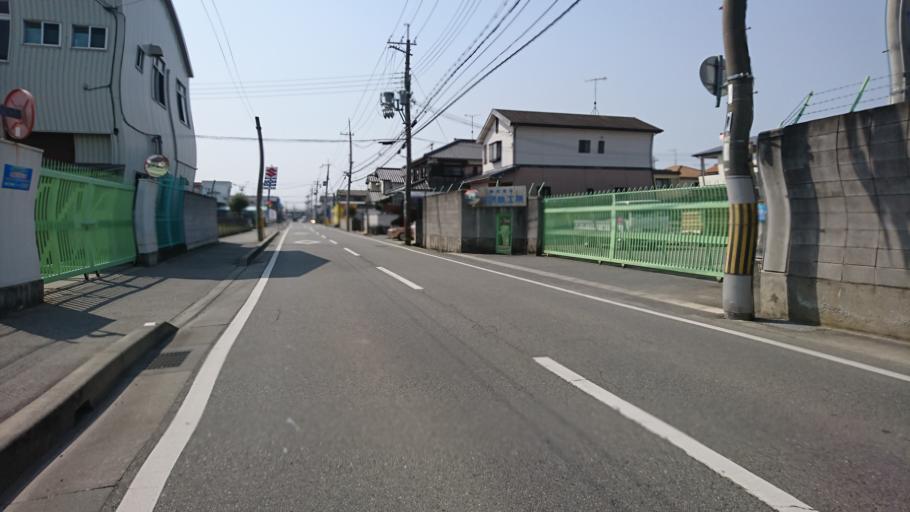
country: JP
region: Hyogo
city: Shirahamacho-usazakiminami
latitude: 34.7883
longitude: 134.7511
